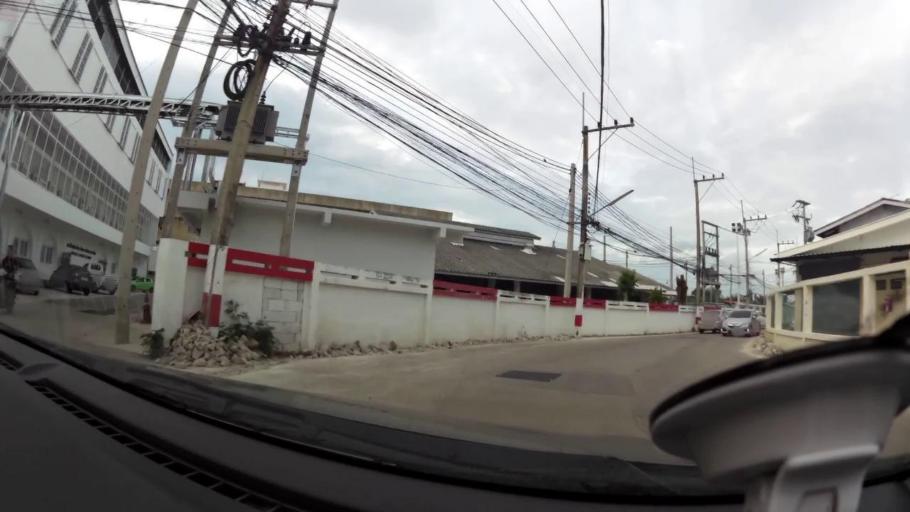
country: TH
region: Prachuap Khiri Khan
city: Hua Hin
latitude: 12.5929
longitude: 99.9528
